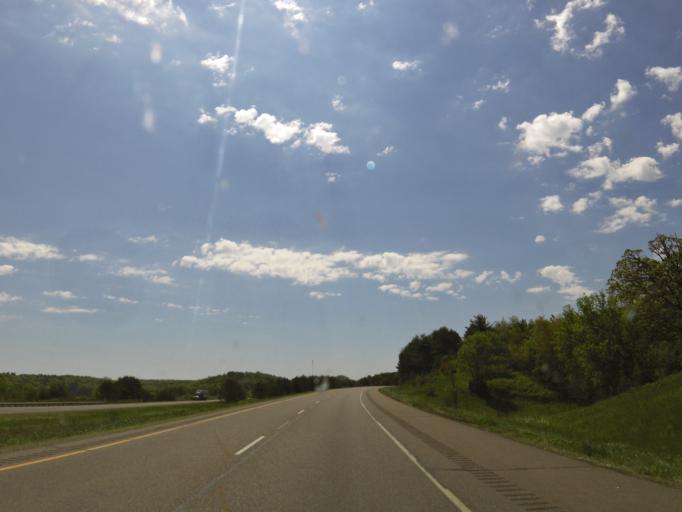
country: US
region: Wisconsin
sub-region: Trempealeau County
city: Osseo
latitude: 44.4522
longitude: -91.0847
